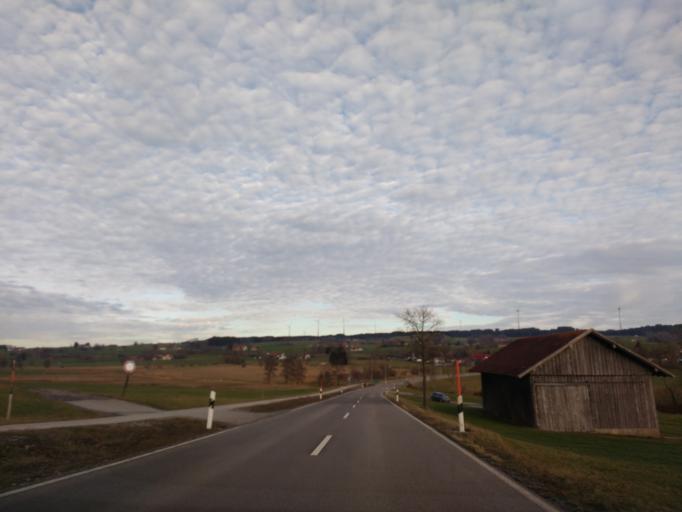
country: DE
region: Bavaria
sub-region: Swabia
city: Wildpoldsried
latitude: 47.7688
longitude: 10.3898
